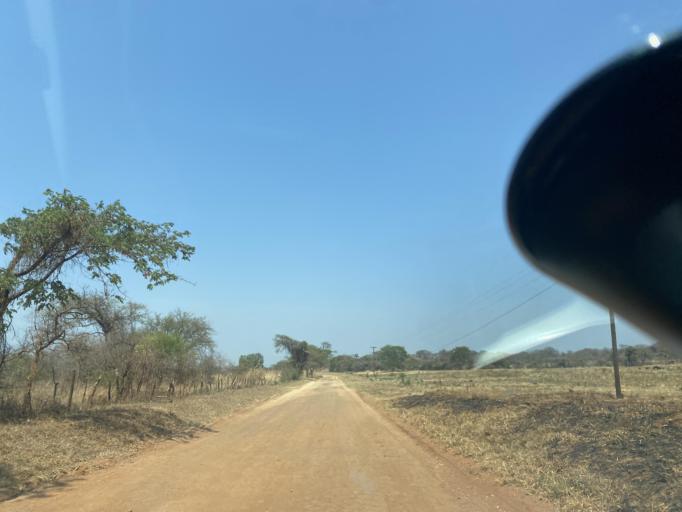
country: ZM
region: Lusaka
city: Kafue
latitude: -15.5427
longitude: 28.0742
